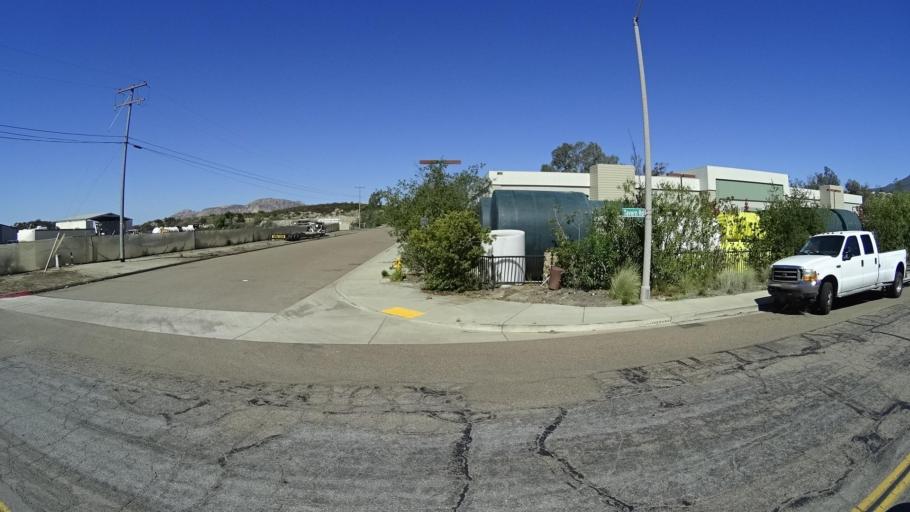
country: US
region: California
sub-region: San Diego County
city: Alpine
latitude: 32.8420
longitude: -116.7863
